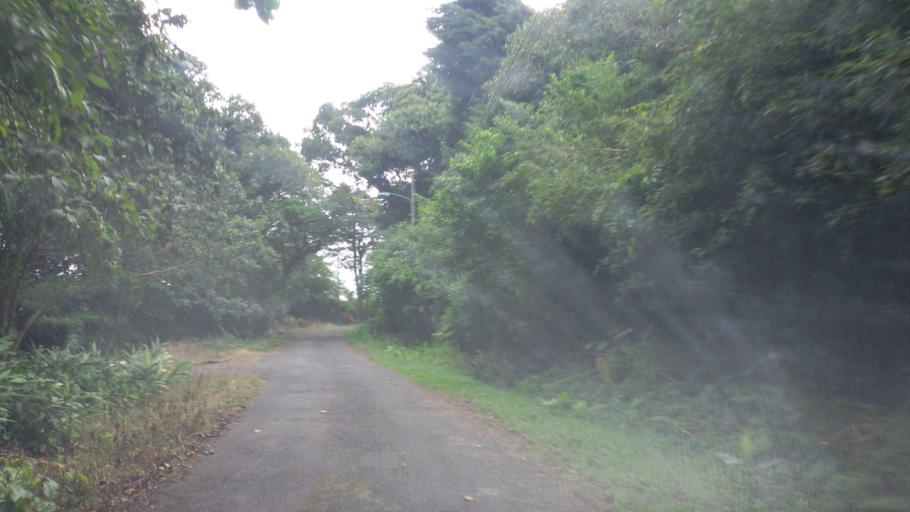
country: CR
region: Heredia
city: Angeles
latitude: 10.0357
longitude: -84.0126
